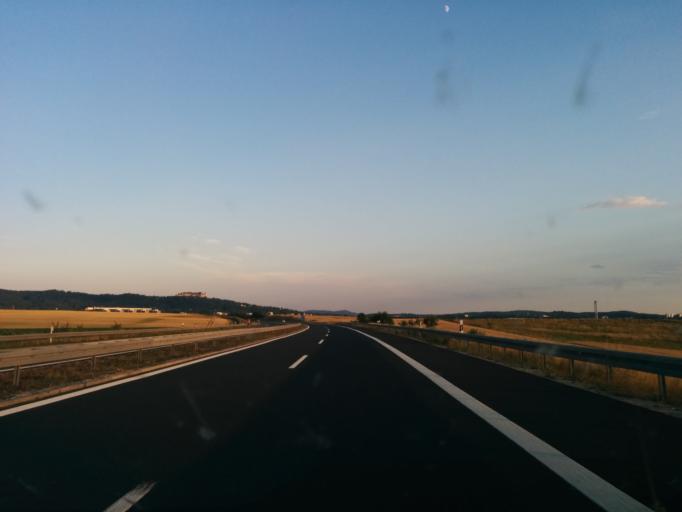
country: DE
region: Bavaria
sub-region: Upper Franconia
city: Lautertal
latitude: 50.3002
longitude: 10.9628
